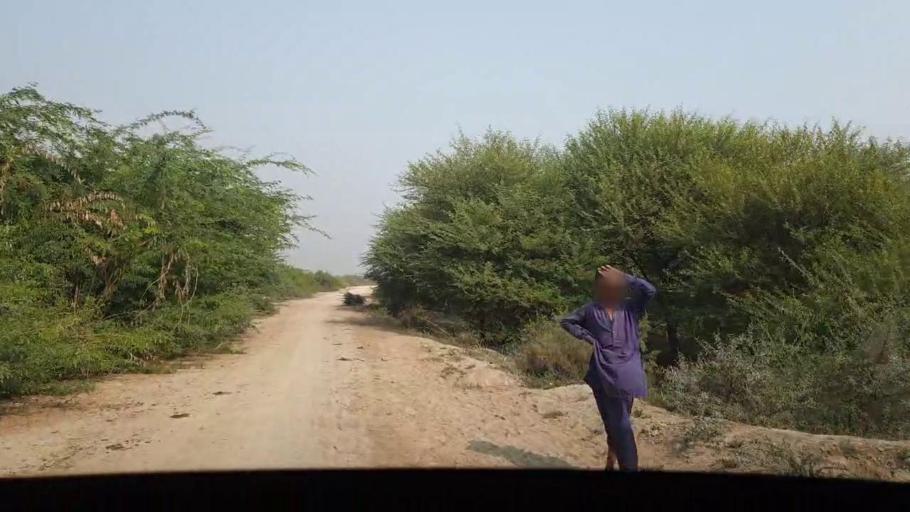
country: PK
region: Sindh
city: Jati
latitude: 24.4334
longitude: 68.4357
